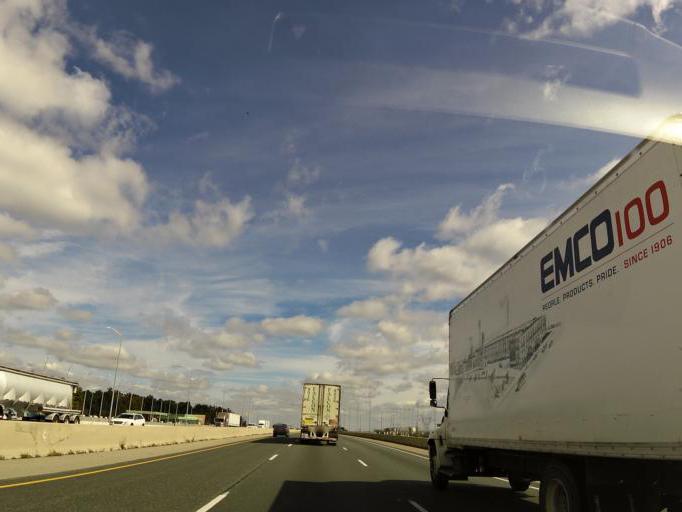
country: CA
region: Ontario
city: Dorchester
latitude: 42.9727
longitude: -80.9713
